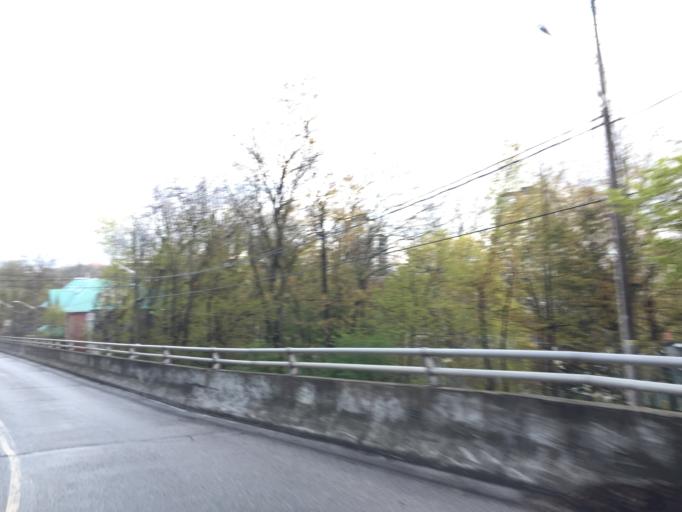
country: CA
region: Ontario
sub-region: Wellington County
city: Guelph
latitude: 43.5498
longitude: -80.2444
